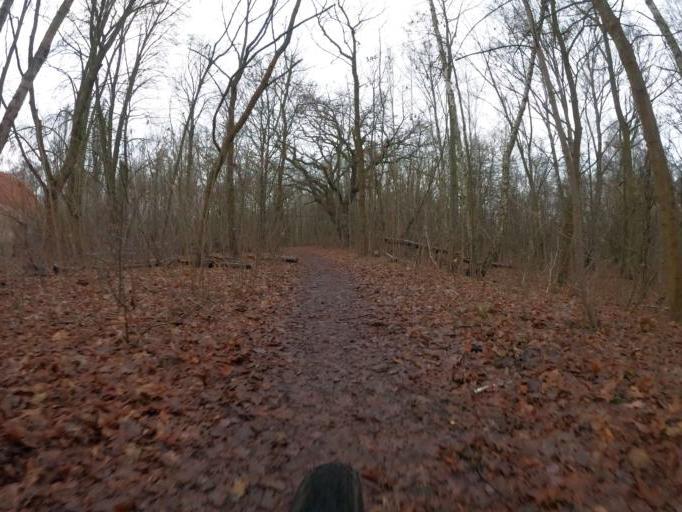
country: DE
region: Brandenburg
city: Schulzendorf
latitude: 52.3647
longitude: 13.5969
